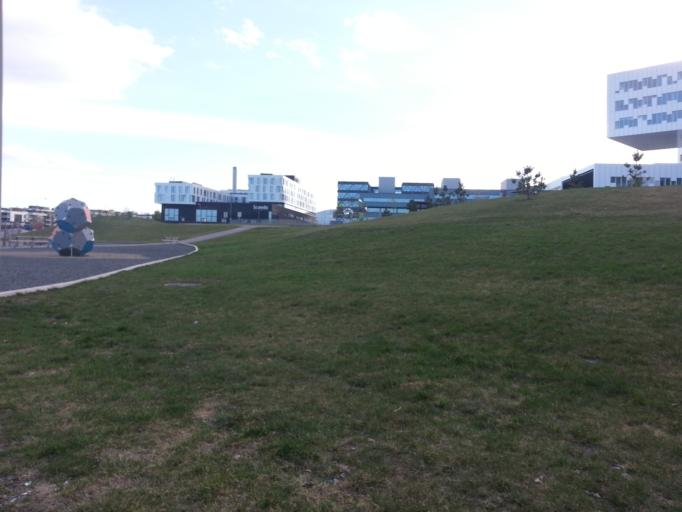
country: NO
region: Akershus
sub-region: Baerum
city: Lysaker
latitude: 59.8957
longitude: 10.6327
